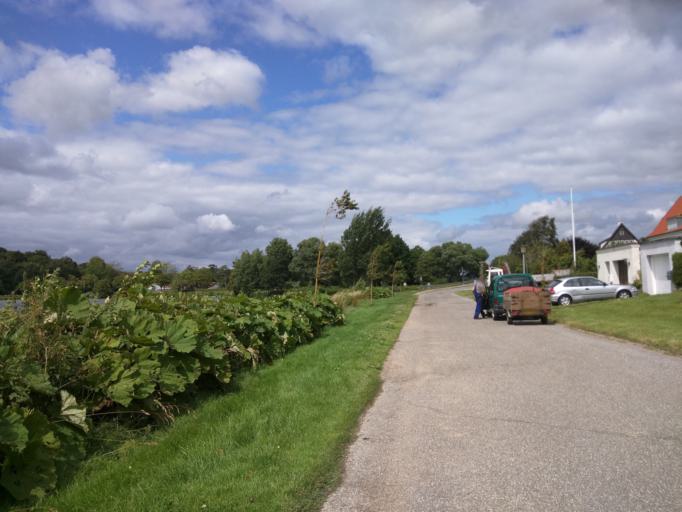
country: DK
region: Central Jutland
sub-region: Viborg Kommune
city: Viborg
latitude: 56.4480
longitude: 9.4237
